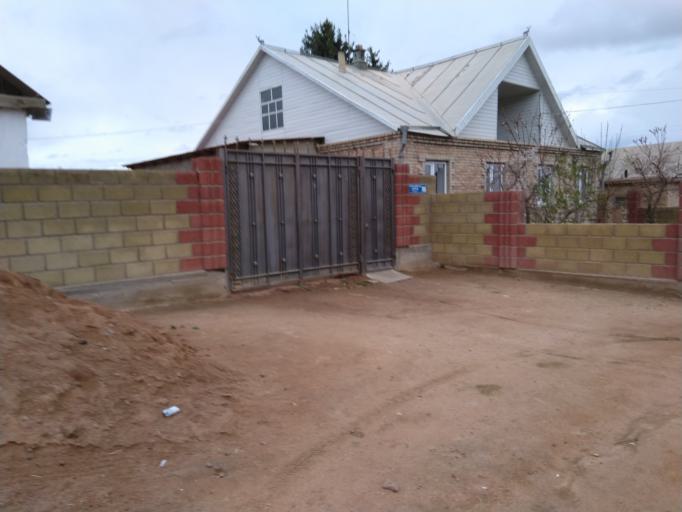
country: KG
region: Ysyk-Koel
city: Bokombayevskoye
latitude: 42.1096
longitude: 76.9826
